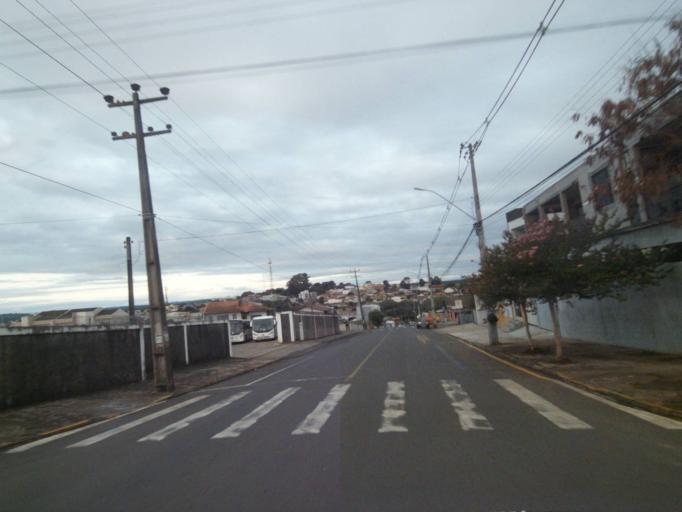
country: BR
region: Parana
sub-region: Telemaco Borba
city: Telemaco Borba
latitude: -24.3312
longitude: -50.6295
